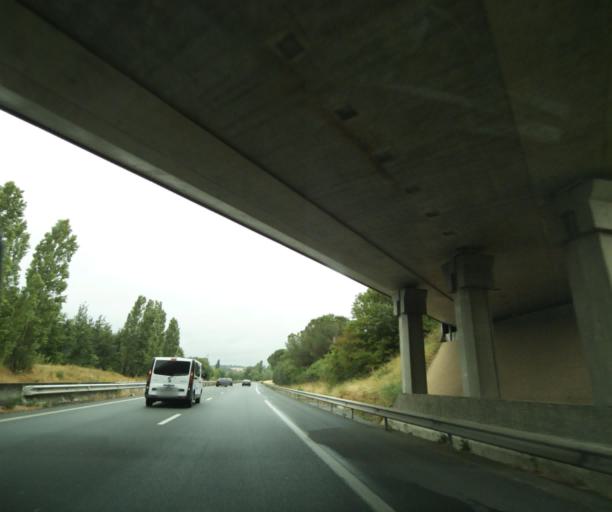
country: FR
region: Midi-Pyrenees
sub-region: Departement de la Haute-Garonne
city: Gragnague
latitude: 43.6855
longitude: 1.5639
